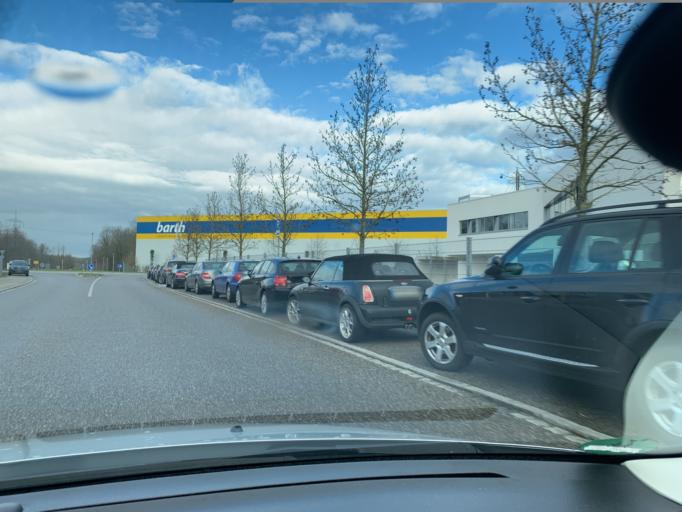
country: DE
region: Baden-Wuerttemberg
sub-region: Freiburg Region
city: Umkirch
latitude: 48.0415
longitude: 7.7585
